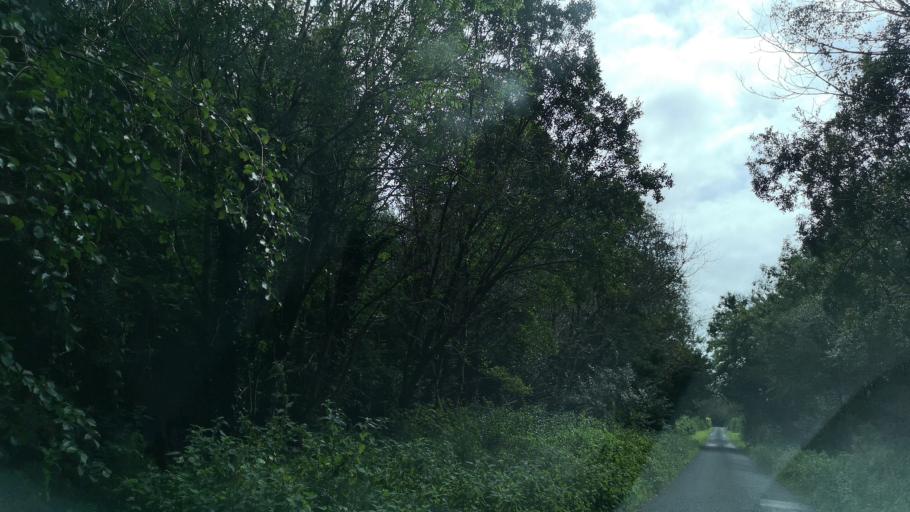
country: IE
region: Connaught
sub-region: County Galway
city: Athenry
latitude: 53.2942
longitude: -8.6631
